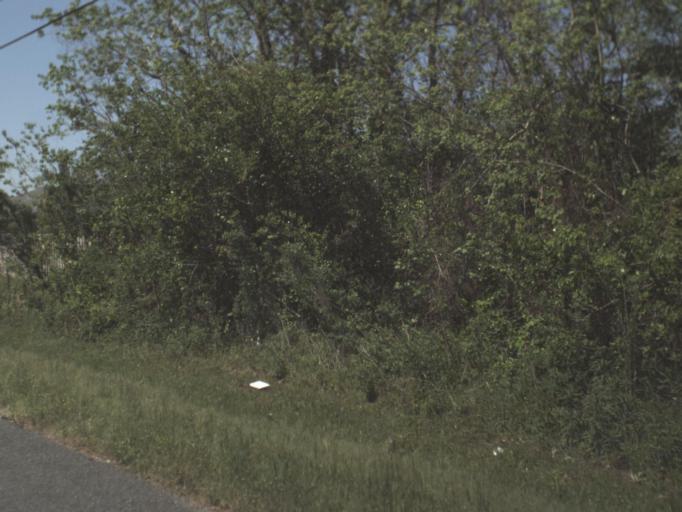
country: US
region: Florida
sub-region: Escambia County
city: Bellview
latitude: 30.5169
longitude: -87.3772
